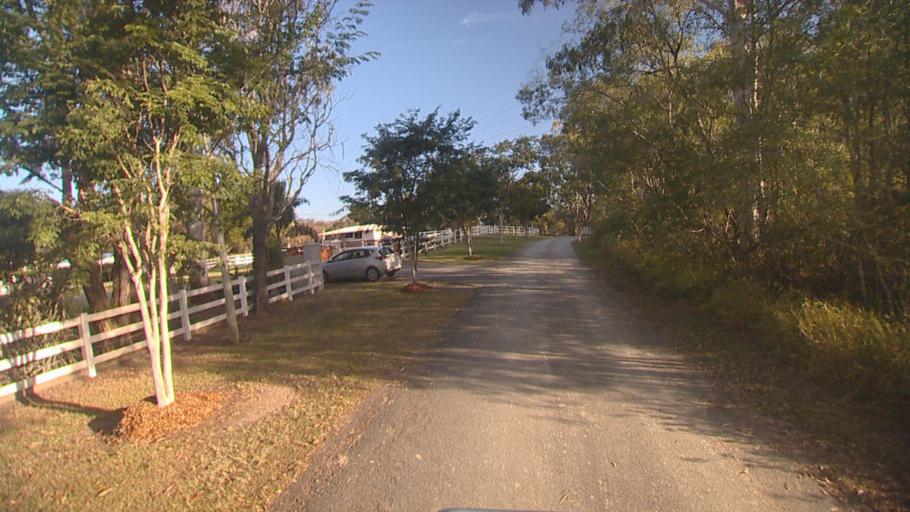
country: AU
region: Queensland
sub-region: Logan
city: Windaroo
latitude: -27.7928
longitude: 153.1794
